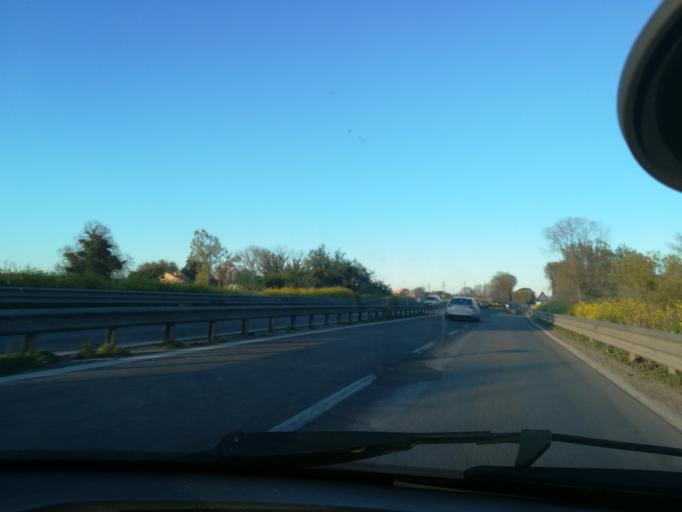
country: IT
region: The Marches
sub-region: Provincia di Macerata
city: Santa Maria Apparente
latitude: 43.2850
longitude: 13.6981
